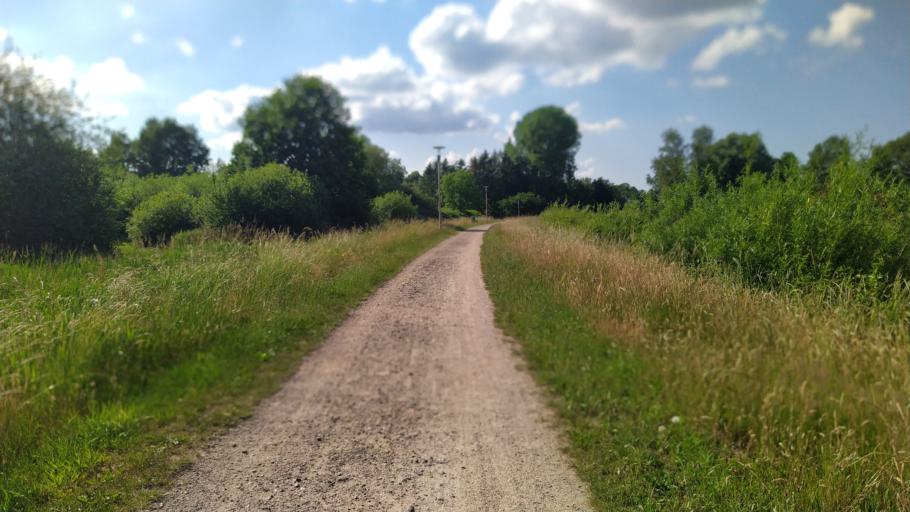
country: DE
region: Lower Saxony
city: Lintig
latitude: 53.6218
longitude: 8.8492
